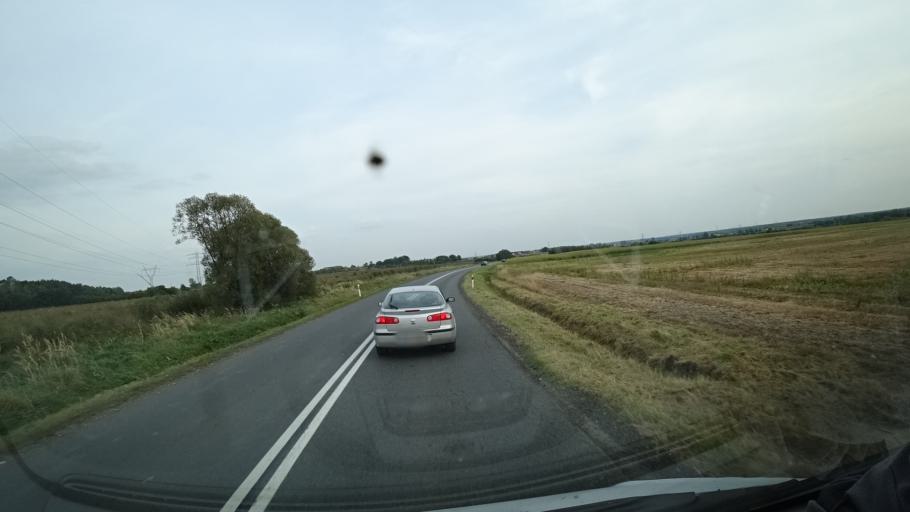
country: PL
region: Silesian Voivodeship
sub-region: Powiat gliwicki
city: Toszek
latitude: 50.3960
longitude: 18.5185
